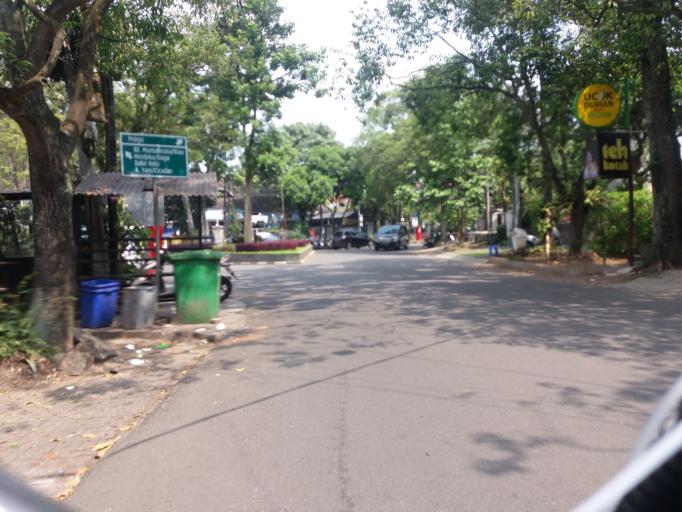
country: ID
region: West Java
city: Bandung
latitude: -6.9043
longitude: 107.6205
